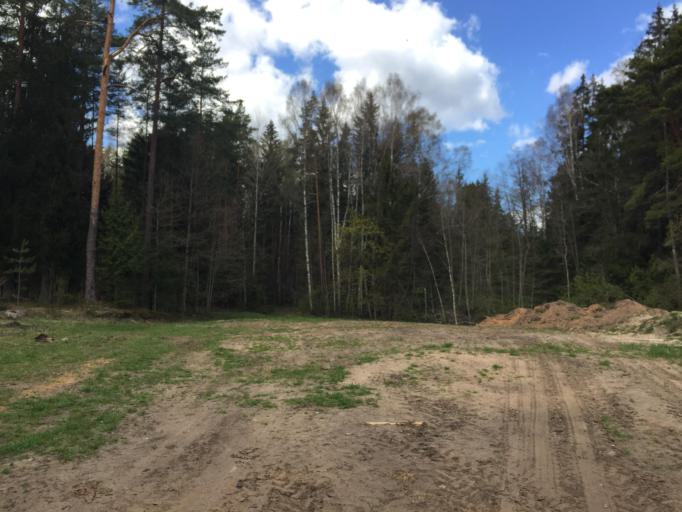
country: LV
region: Baldone
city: Baldone
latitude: 56.7471
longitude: 24.3832
